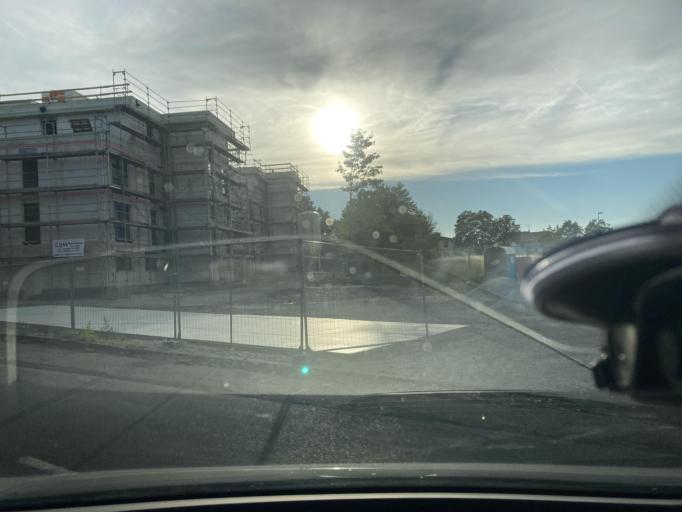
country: DE
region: Rheinland-Pfalz
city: Wirges
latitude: 50.4693
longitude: 7.7983
